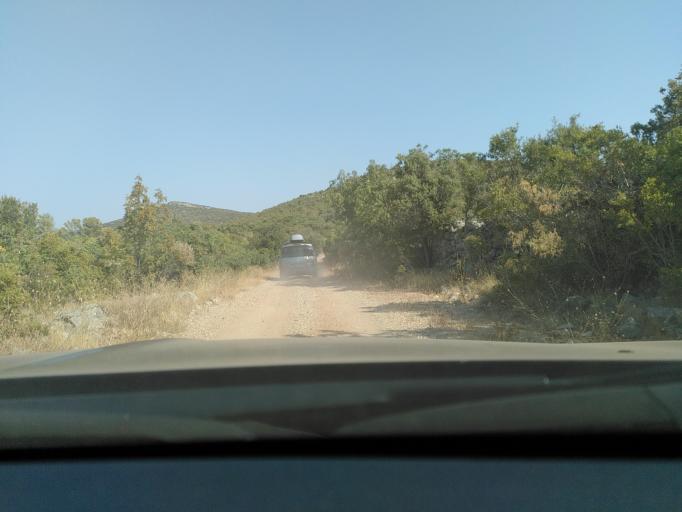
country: HR
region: Splitsko-Dalmatinska
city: Stari Grad
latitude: 43.1608
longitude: 16.5562
